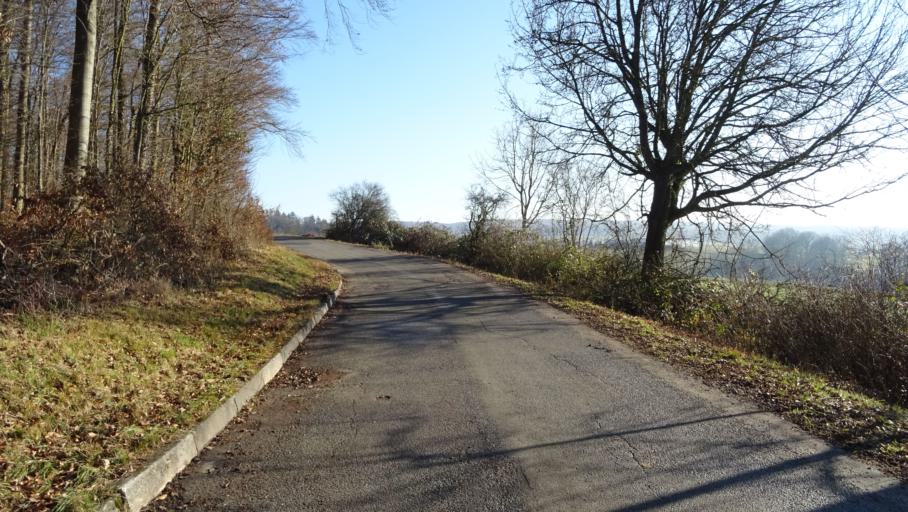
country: DE
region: Baden-Wuerttemberg
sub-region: Karlsruhe Region
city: Binau
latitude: 49.3512
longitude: 9.0378
